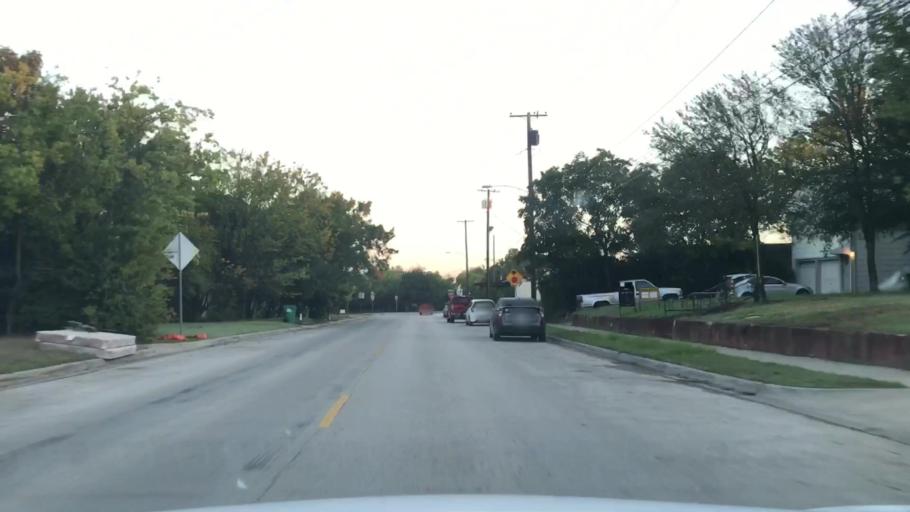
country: US
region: Texas
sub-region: Denton County
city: Denton
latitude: 33.2175
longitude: -97.1506
